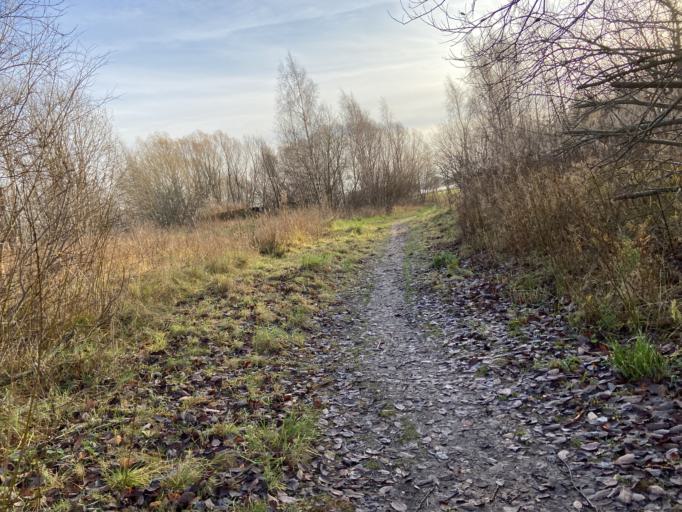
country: EE
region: Harju
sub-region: Tallinna linn
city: Tallinn
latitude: 59.4743
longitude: 24.7205
